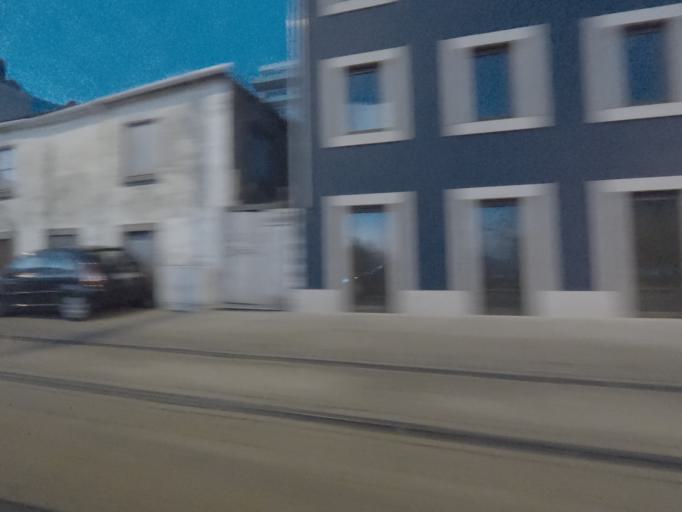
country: PT
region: Porto
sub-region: Vila Nova de Gaia
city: Canidelo
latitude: 41.1480
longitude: -8.6634
